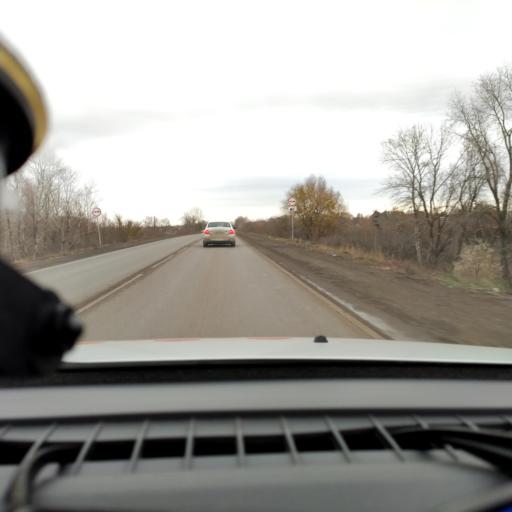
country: RU
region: Samara
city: Samara
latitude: 53.1046
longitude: 50.1370
